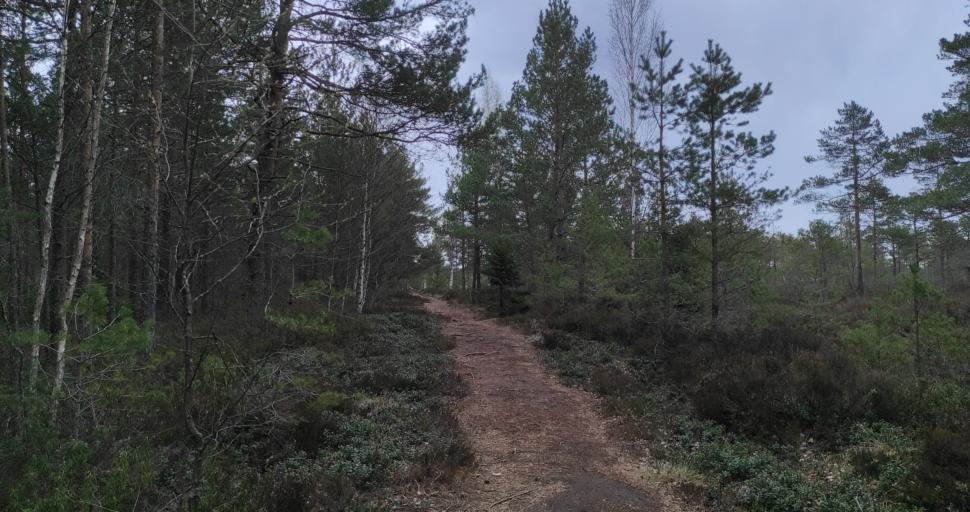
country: LV
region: Dundaga
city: Dundaga
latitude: 57.3471
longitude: 22.1498
